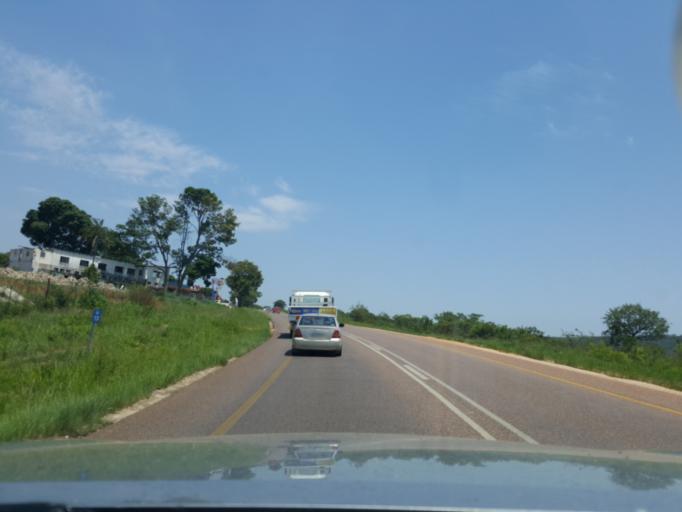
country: ZA
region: Limpopo
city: Thulamahashi
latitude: -24.8944
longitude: 31.1059
